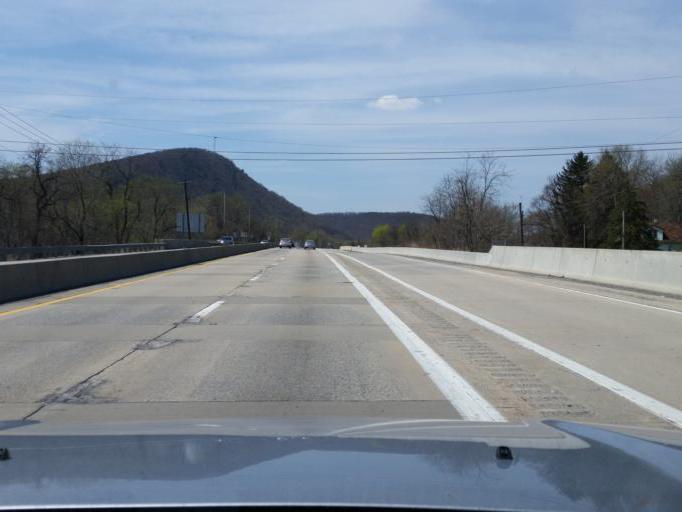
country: US
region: Pennsylvania
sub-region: Perry County
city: Duncannon
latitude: 40.3794
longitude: -77.0088
